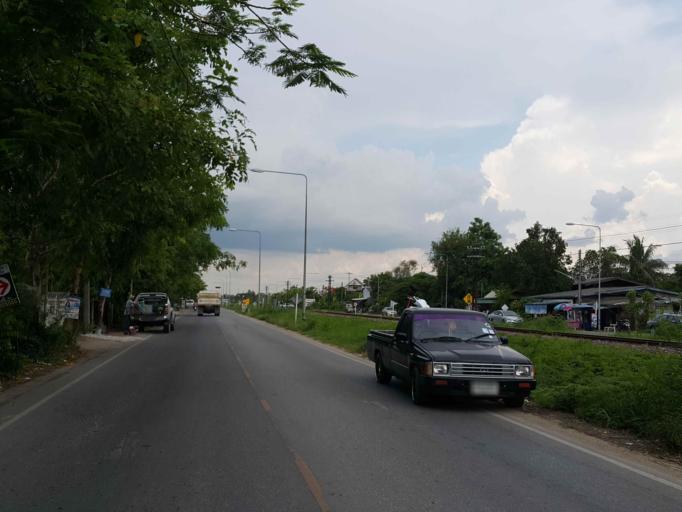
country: TH
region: Chiang Mai
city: Saraphi
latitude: 18.7490
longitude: 99.0252
